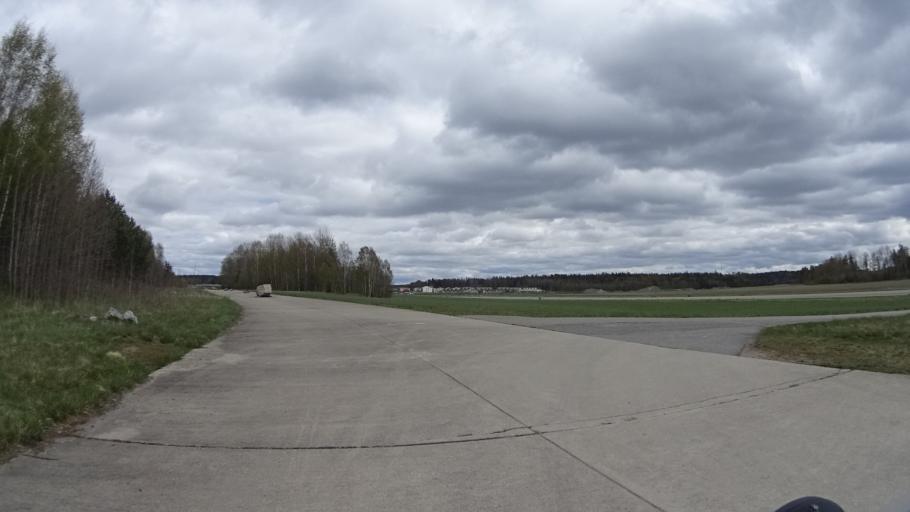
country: SE
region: Stockholm
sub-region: Botkyrka Kommun
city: Tullinge
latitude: 59.1778
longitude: 17.8981
